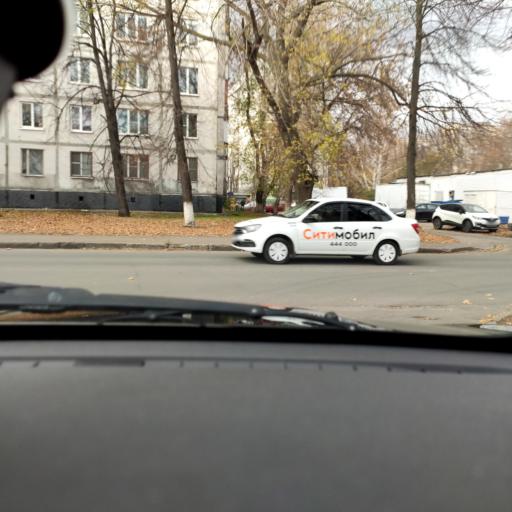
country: RU
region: Samara
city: Tol'yatti
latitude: 53.5151
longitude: 49.2682
